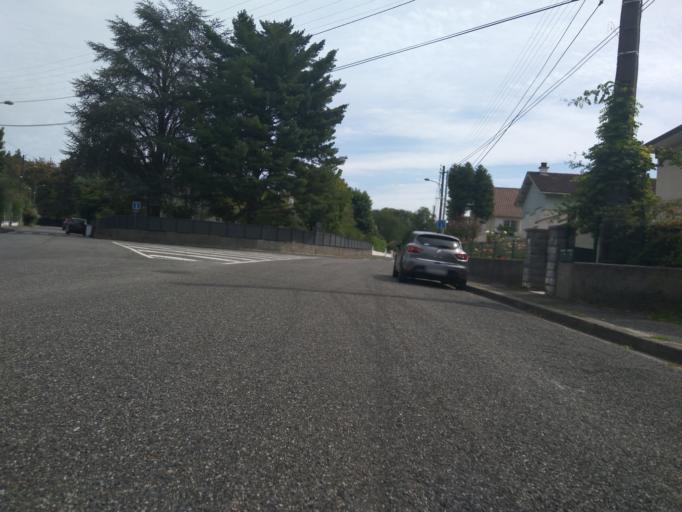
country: FR
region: Aquitaine
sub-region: Departement des Pyrenees-Atlantiques
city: Bizanos
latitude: 43.2939
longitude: -0.3499
